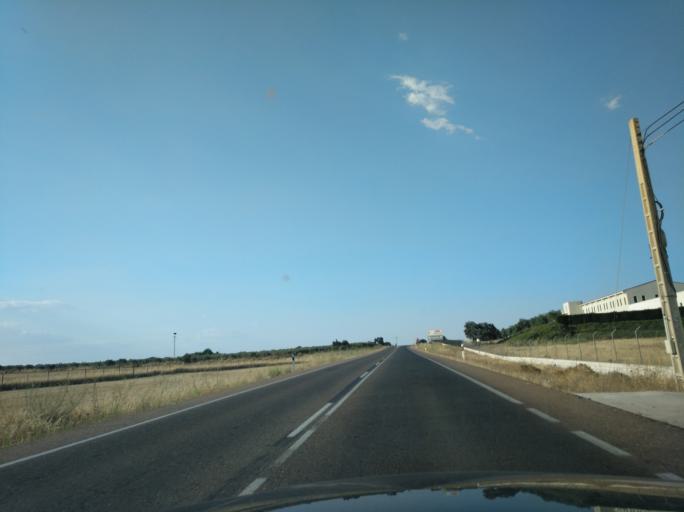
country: ES
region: Extremadura
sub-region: Provincia de Badajoz
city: Olivenza
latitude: 38.7078
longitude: -7.0864
